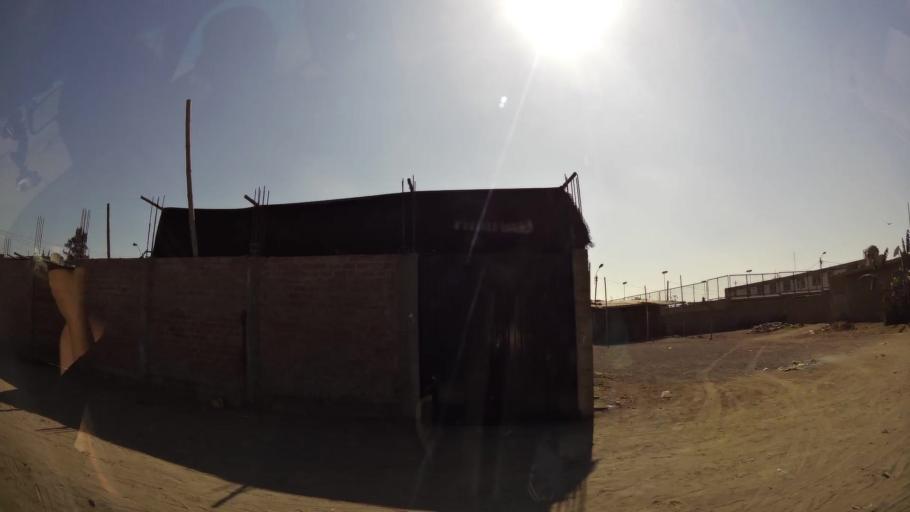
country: PE
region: Ica
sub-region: Provincia de Chincha
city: Chincha Alta
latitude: -13.4137
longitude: -76.1274
